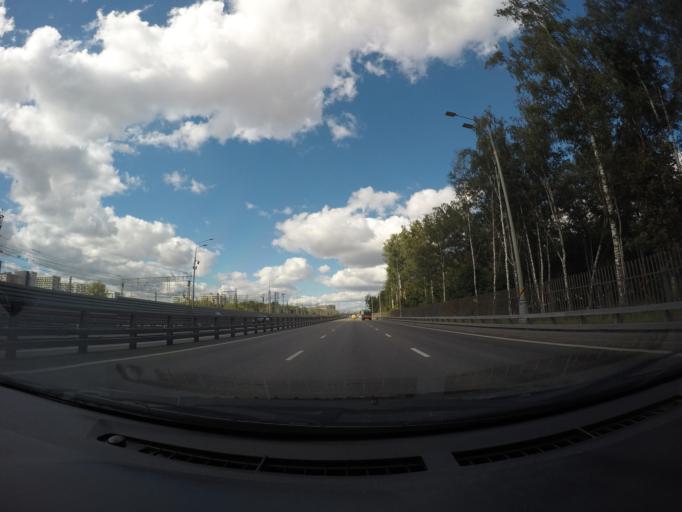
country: RU
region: Moscow
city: Perovo
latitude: 55.7278
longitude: 37.7844
